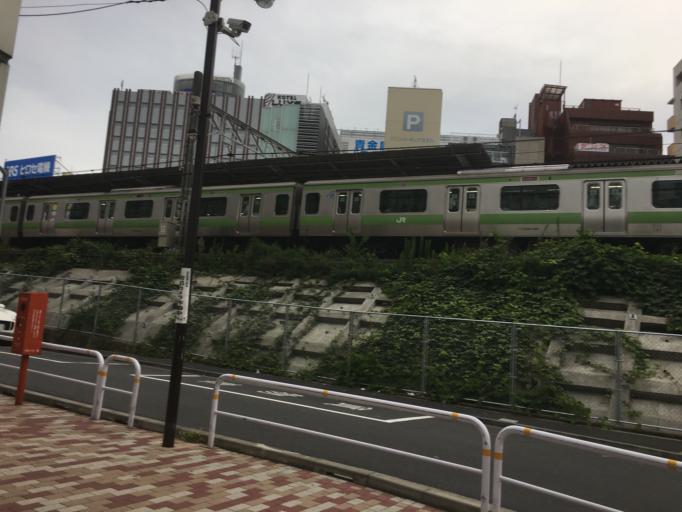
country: JP
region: Tokyo
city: Tokyo
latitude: 35.6275
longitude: 139.7228
